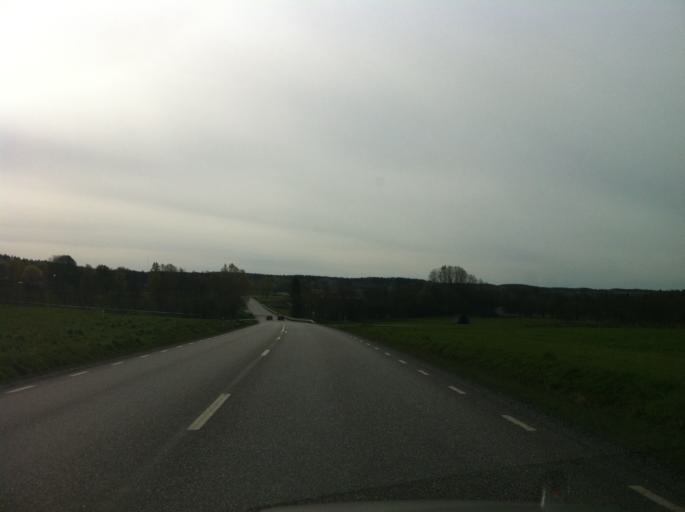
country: SE
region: Vaestra Goetaland
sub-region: Harryda Kommun
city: Ravlanda
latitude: 57.5299
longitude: 12.5352
